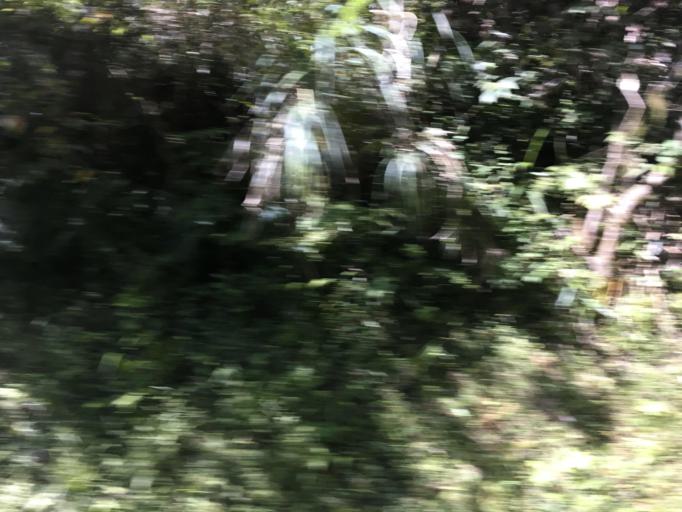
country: TW
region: Taiwan
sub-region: Yilan
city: Yilan
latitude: 24.5344
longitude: 121.5192
